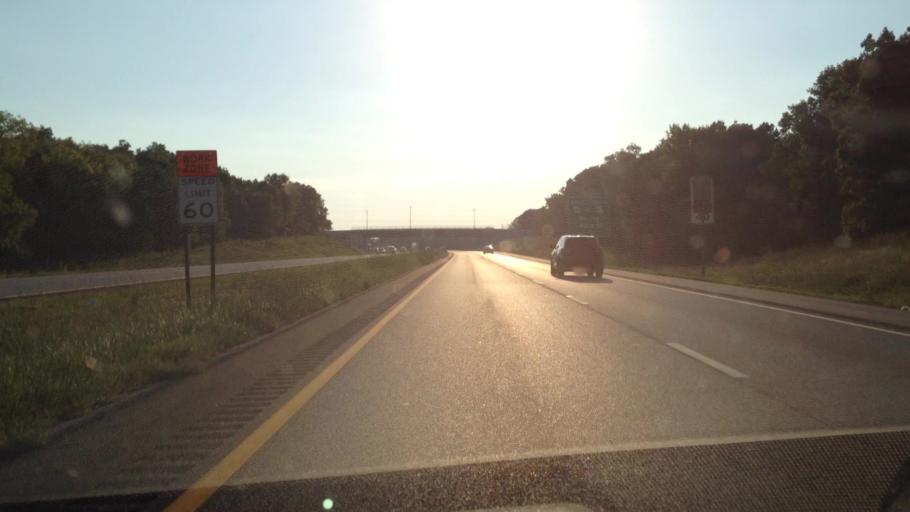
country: US
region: Missouri
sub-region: Jasper County
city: Joplin
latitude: 37.0459
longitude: -94.4924
